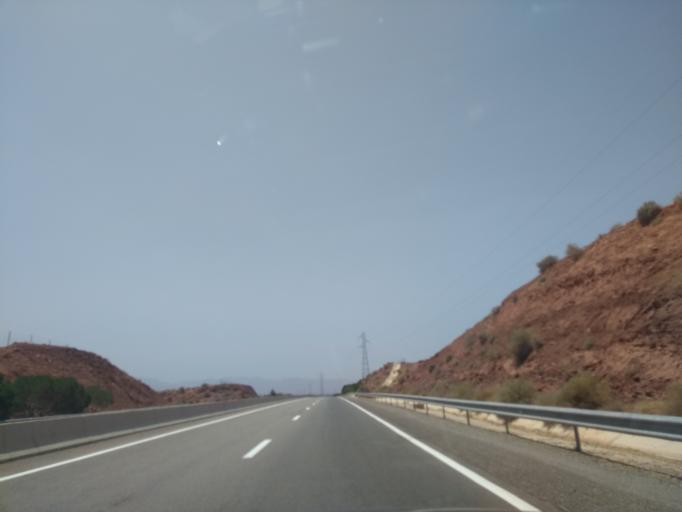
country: MA
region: Marrakech-Tensift-Al Haouz
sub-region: Chichaoua
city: Timezgadiouine
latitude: 30.8958
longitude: -9.0751
